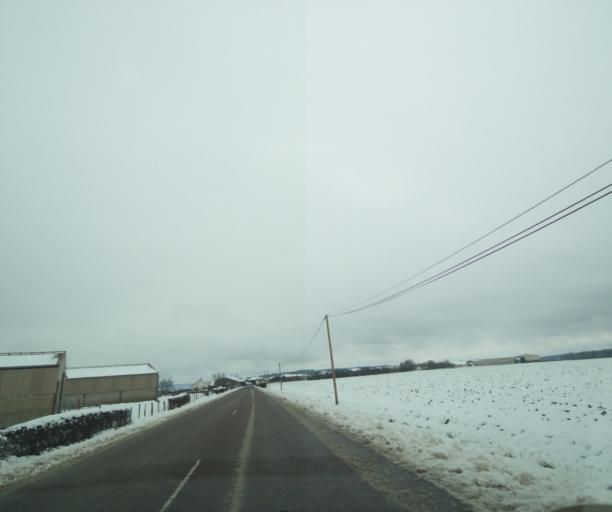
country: FR
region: Champagne-Ardenne
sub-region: Departement de la Haute-Marne
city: Montier-en-Der
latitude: 48.4447
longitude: 4.8016
